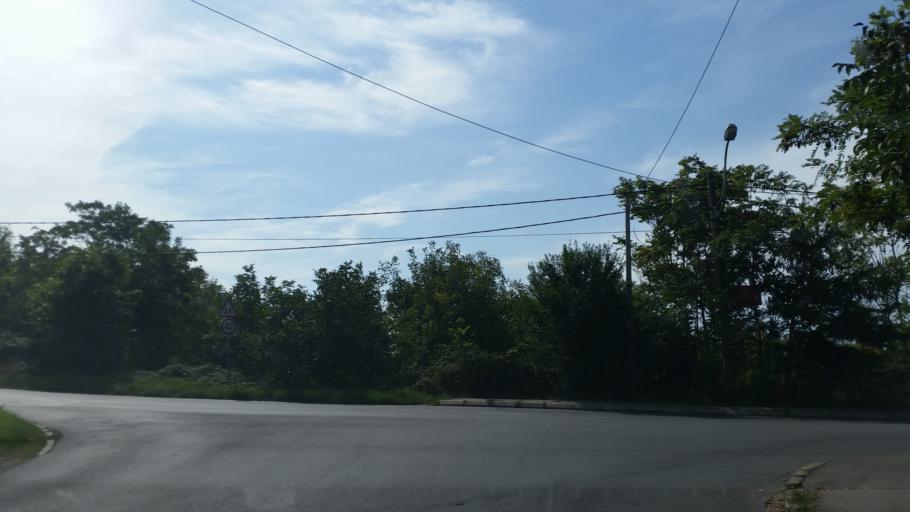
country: RS
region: Central Serbia
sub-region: Belgrade
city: Palilula
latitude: 44.8094
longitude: 20.5015
